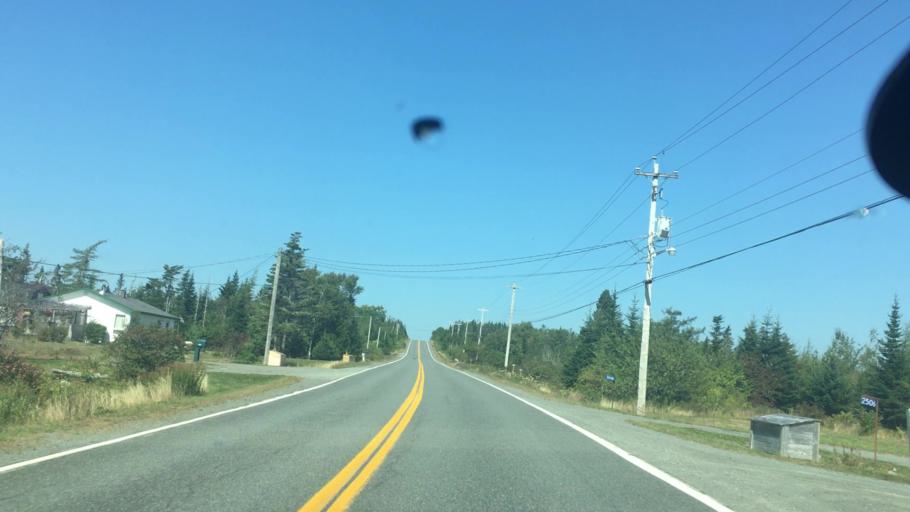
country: CA
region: Nova Scotia
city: Antigonish
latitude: 45.0008
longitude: -62.0998
